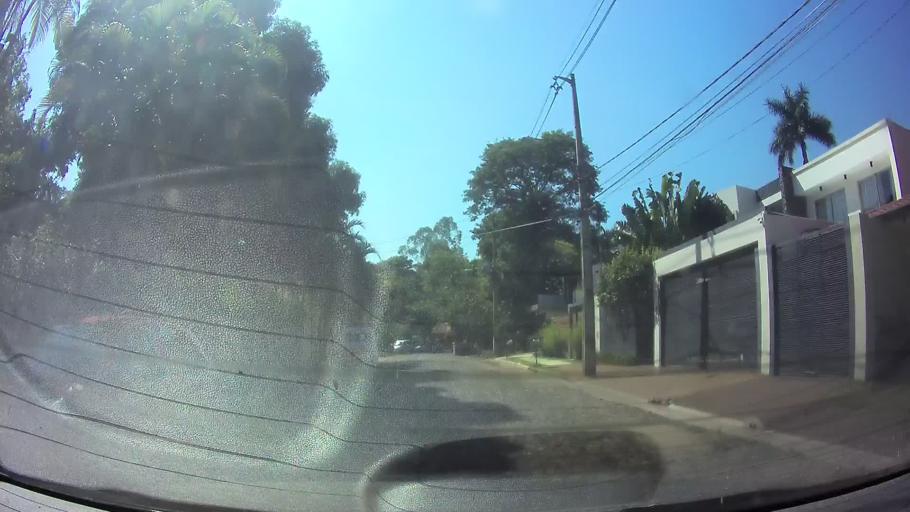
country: PY
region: Central
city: Fernando de la Mora
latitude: -25.2866
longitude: -57.5609
